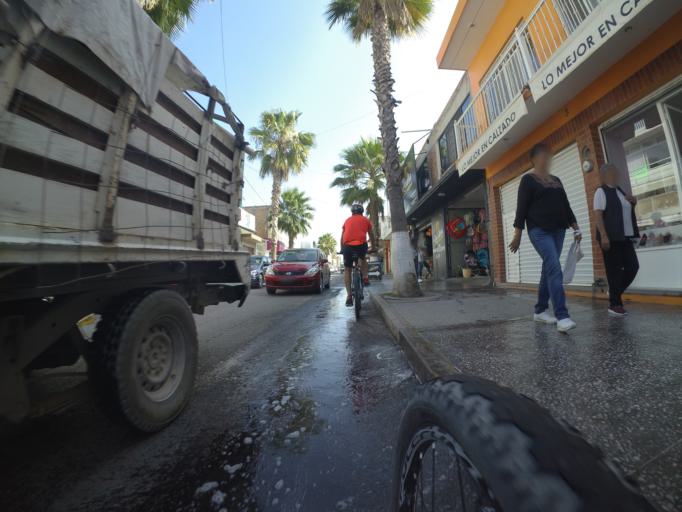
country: MX
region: Aguascalientes
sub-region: Jesus Maria
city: Jesus Maria
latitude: 21.9627
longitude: -102.3433
